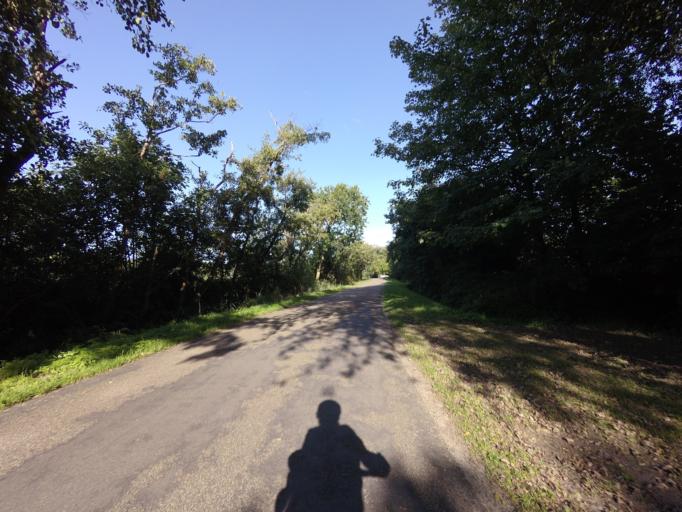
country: NL
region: Friesland
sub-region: Gemeente Terschelling
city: West-Terschelling
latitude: 53.3897
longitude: 5.2748
